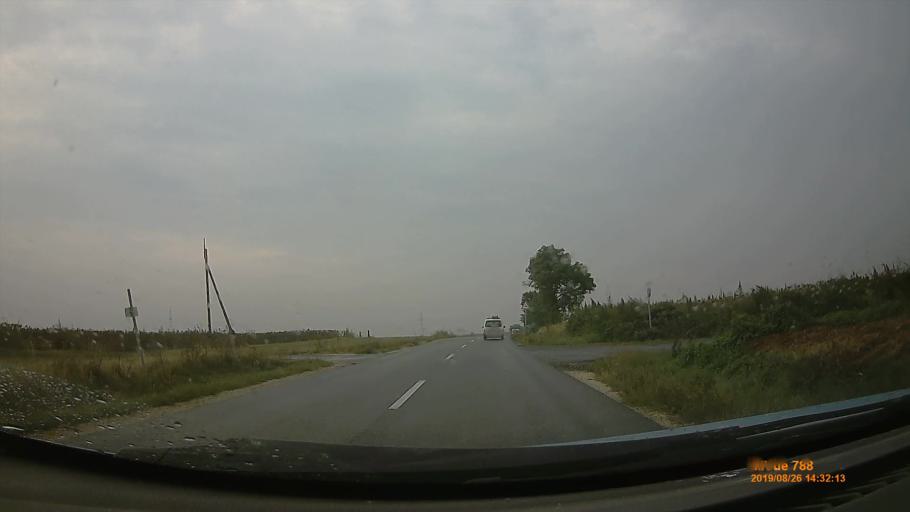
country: HU
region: Fejer
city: Zamoly
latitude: 47.2875
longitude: 18.4215
